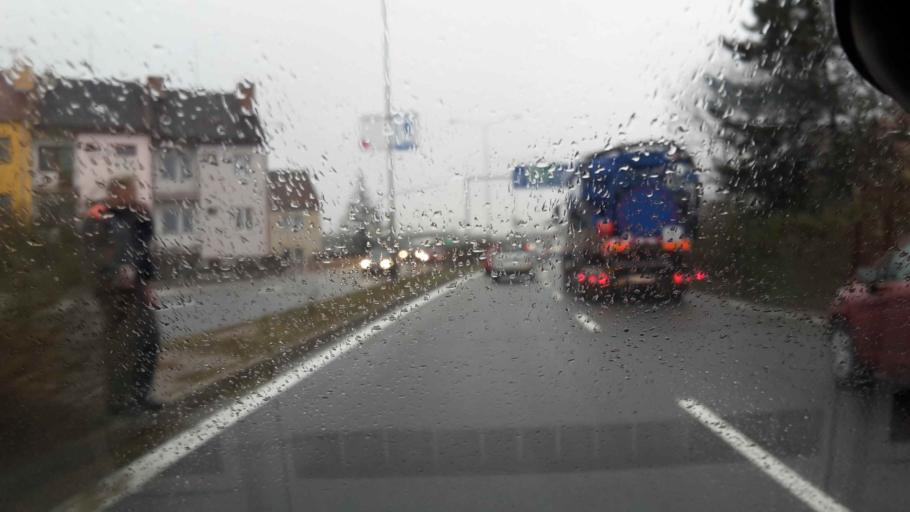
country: CZ
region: South Moravian
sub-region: Mesto Brno
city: Brno
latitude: 49.1920
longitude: 16.6479
